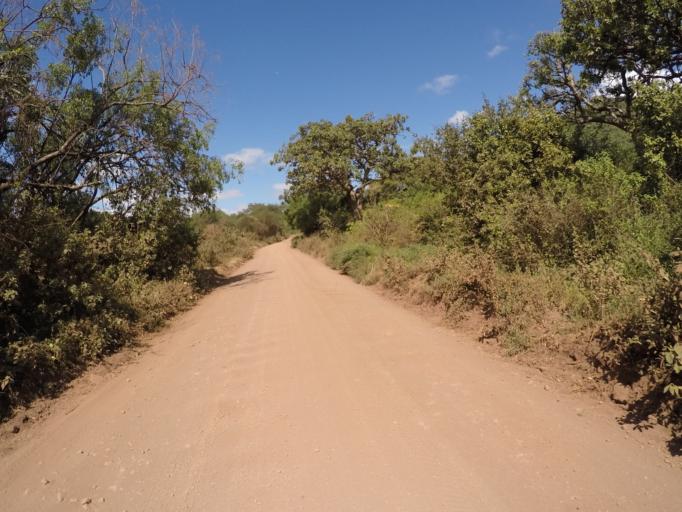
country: TZ
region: Arusha
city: Mto wa Mbu
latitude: -3.3898
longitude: 35.8256
